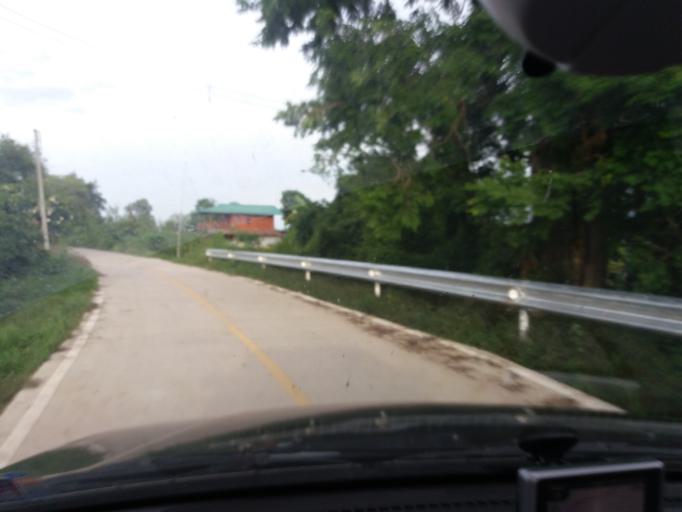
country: TH
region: Suphan Buri
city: Doembang Nangbuat
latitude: 14.8282
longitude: 100.1387
